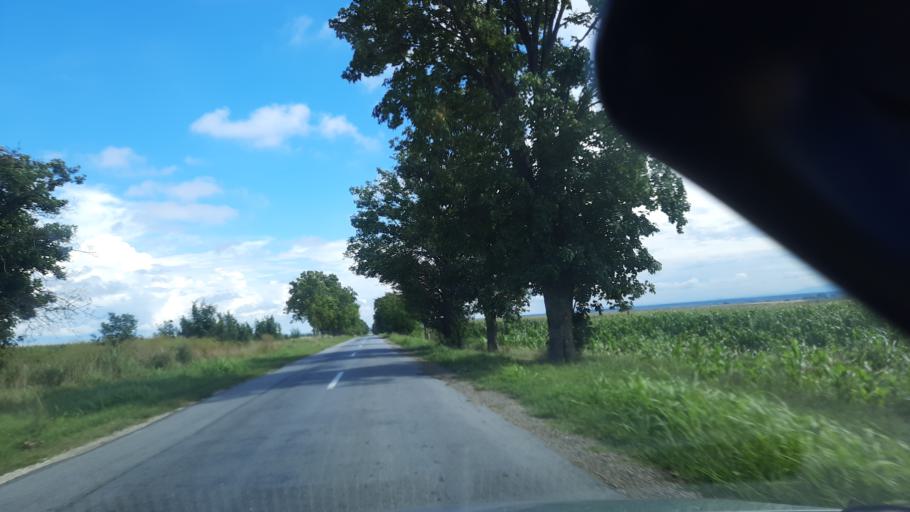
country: RS
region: Autonomna Pokrajina Vojvodina
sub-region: Sremski Okrug
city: Sremska Mitrovica
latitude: 45.0785
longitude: 19.5868
